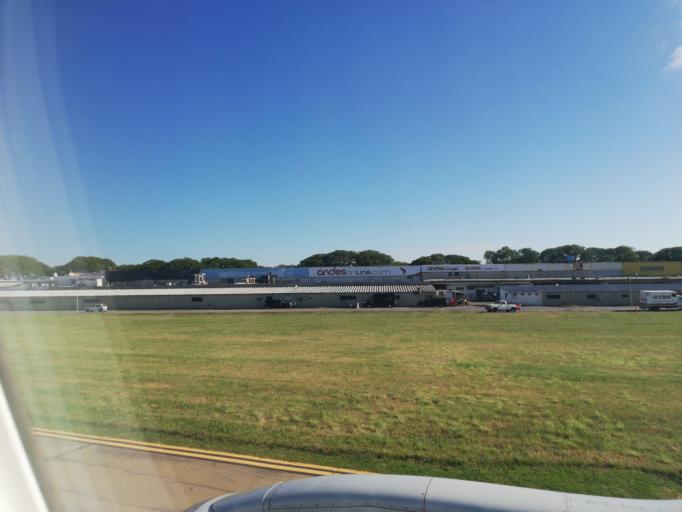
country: AR
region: Buenos Aires F.D.
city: Colegiales
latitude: -34.5559
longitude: -58.4201
